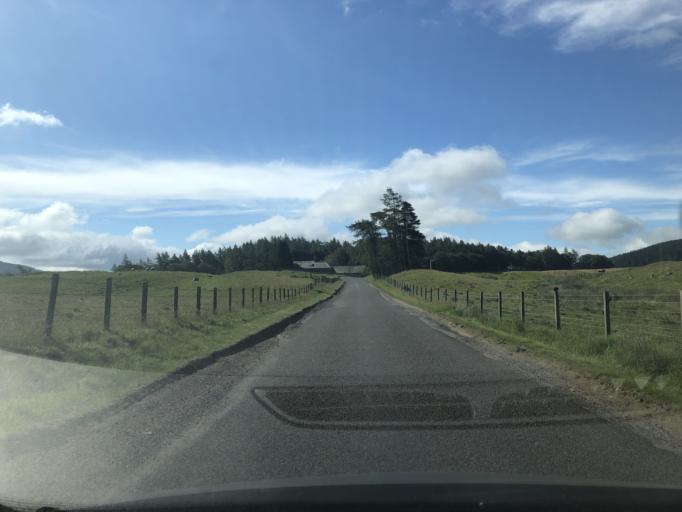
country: GB
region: Scotland
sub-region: Angus
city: Kirriemuir
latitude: 56.7699
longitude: -3.0251
